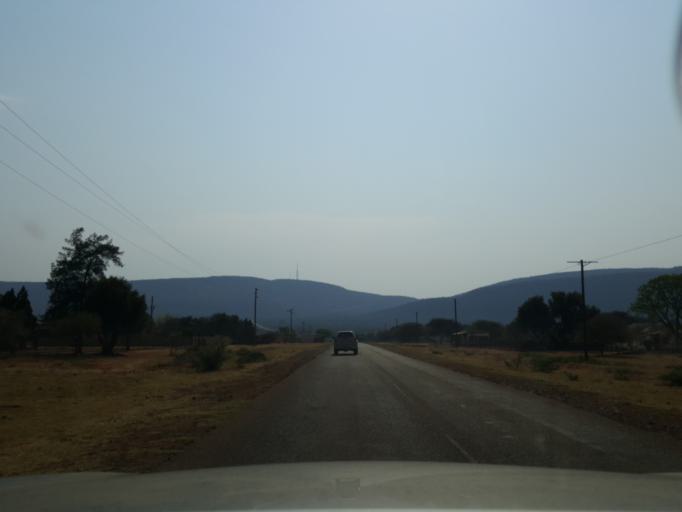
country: BW
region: South East
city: Lobatse
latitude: -25.2958
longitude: 25.8440
